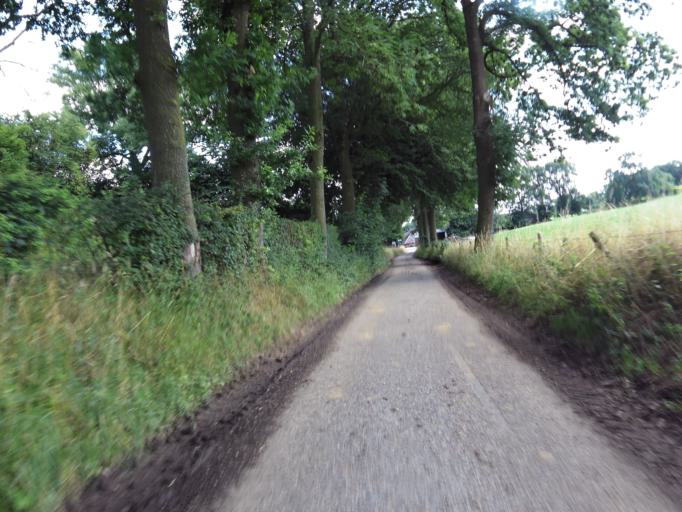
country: NL
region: Limburg
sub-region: Gemeente Voerendaal
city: Ubachsberg
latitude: 50.8386
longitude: 5.9583
